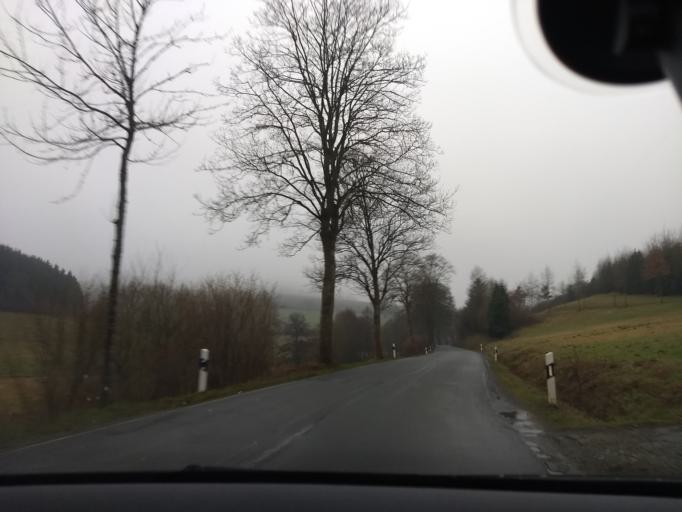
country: DE
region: North Rhine-Westphalia
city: Eslohe
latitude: 51.2451
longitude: 8.1408
